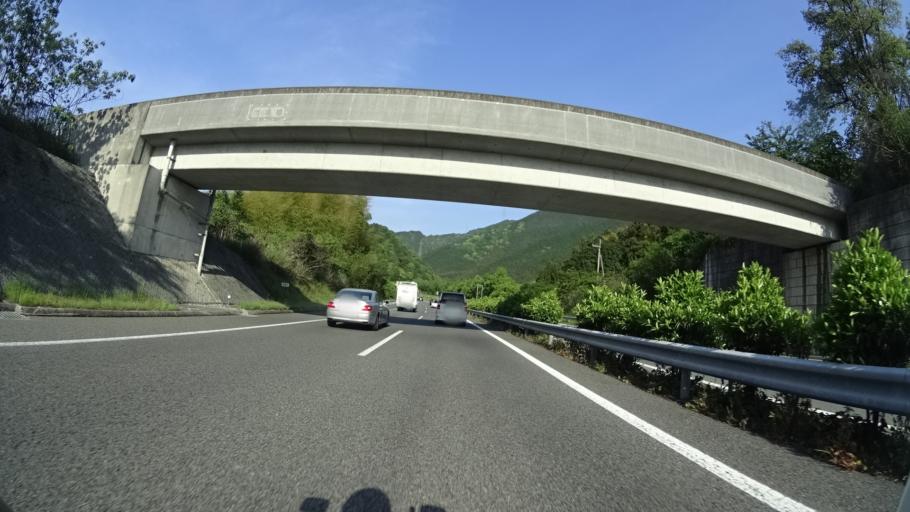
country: JP
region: Ehime
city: Saijo
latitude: 33.8846
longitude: 133.1843
